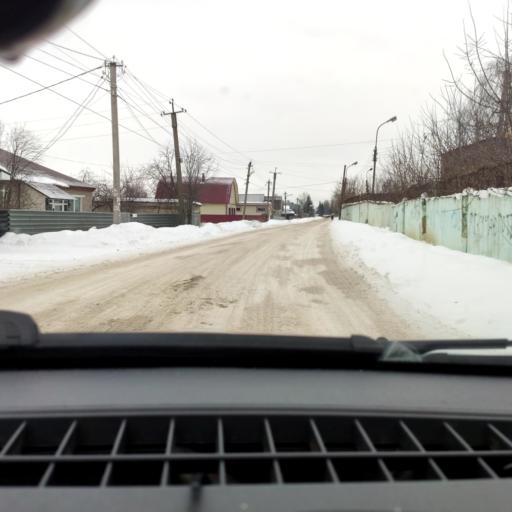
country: RU
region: Bashkortostan
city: Iglino
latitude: 54.8301
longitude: 56.3996
